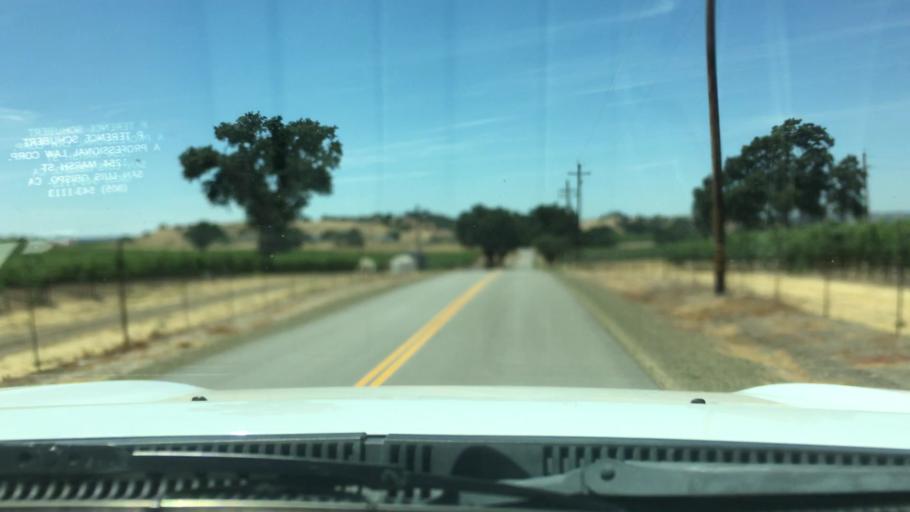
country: US
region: California
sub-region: San Luis Obispo County
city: Paso Robles
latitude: 35.5753
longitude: -120.6252
